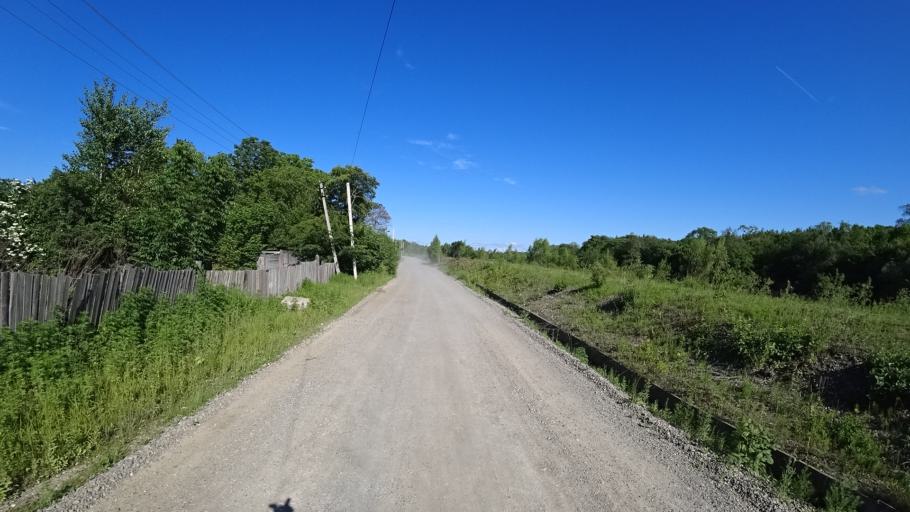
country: RU
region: Khabarovsk Krai
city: Khor
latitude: 47.8864
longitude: 135.0039
